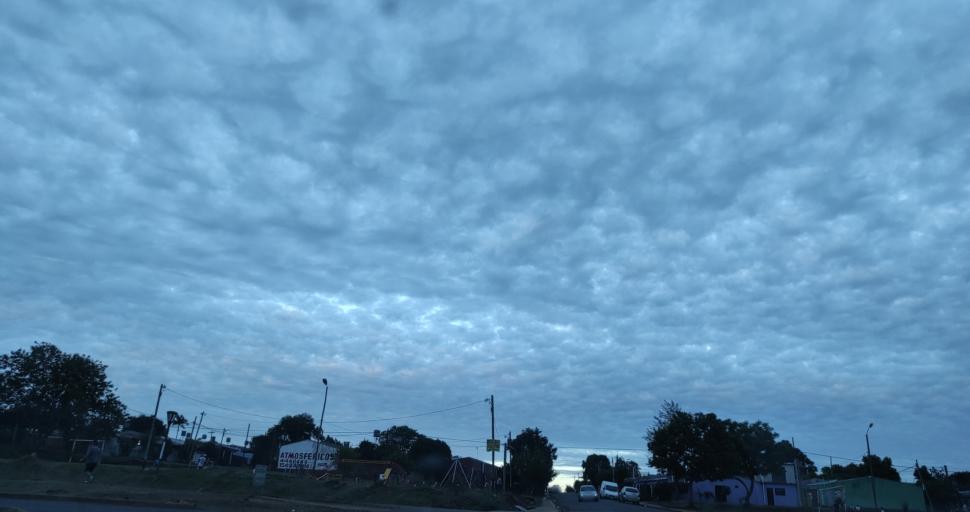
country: AR
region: Misiones
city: Garupa
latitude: -27.4713
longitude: -55.8451
